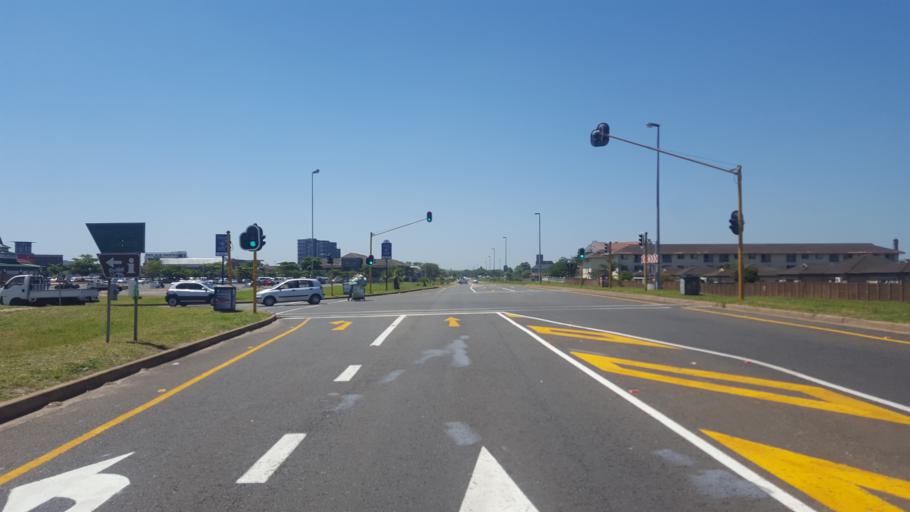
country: ZA
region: KwaZulu-Natal
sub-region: uThungulu District Municipality
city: Richards Bay
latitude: -28.7561
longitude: 32.0529
